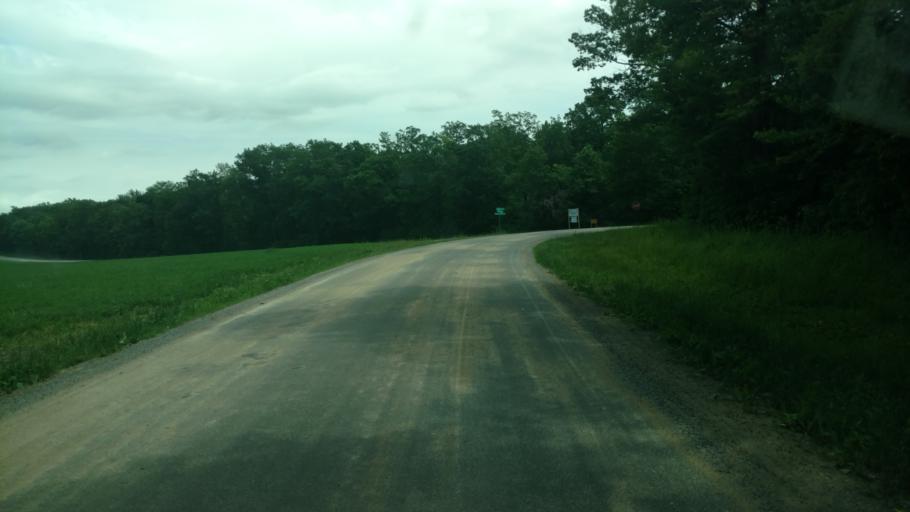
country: US
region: Wisconsin
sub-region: Monroe County
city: Cashton
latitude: 43.6918
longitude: -90.6592
